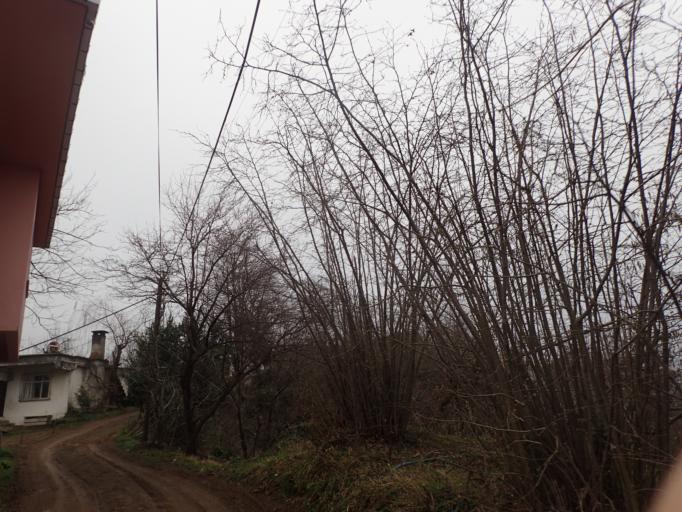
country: TR
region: Ordu
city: Camas
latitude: 40.9175
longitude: 37.5647
